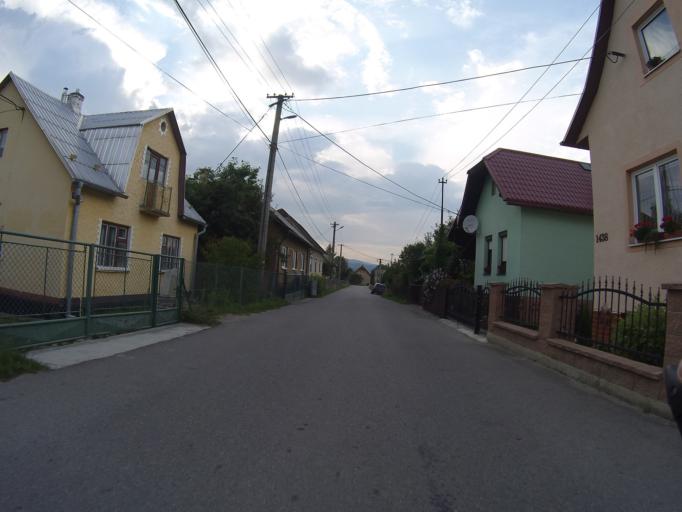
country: SK
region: Nitriansky
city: Puchov
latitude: 49.0398
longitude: 18.3156
